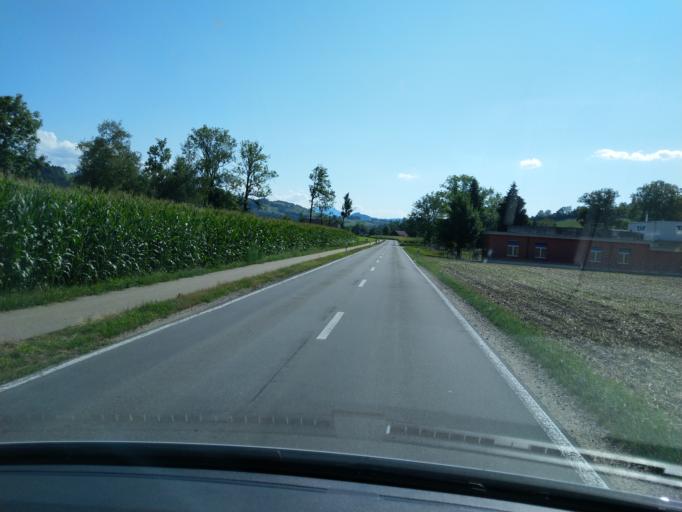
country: CH
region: Lucerne
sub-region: Sursee District
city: Ruswil
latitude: 47.0776
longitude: 8.1095
